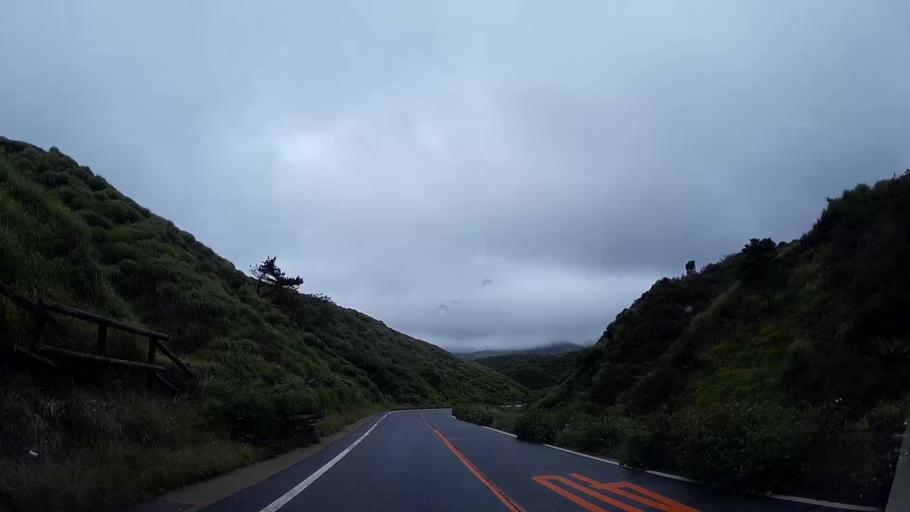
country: JP
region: Kumamoto
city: Aso
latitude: 32.8860
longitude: 131.0569
